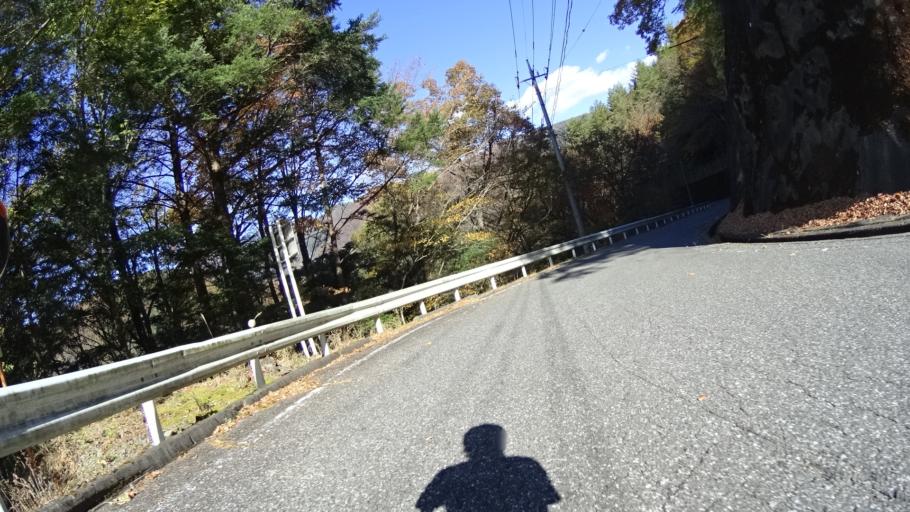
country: JP
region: Yamanashi
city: Otsuki
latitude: 35.7774
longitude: 138.9228
